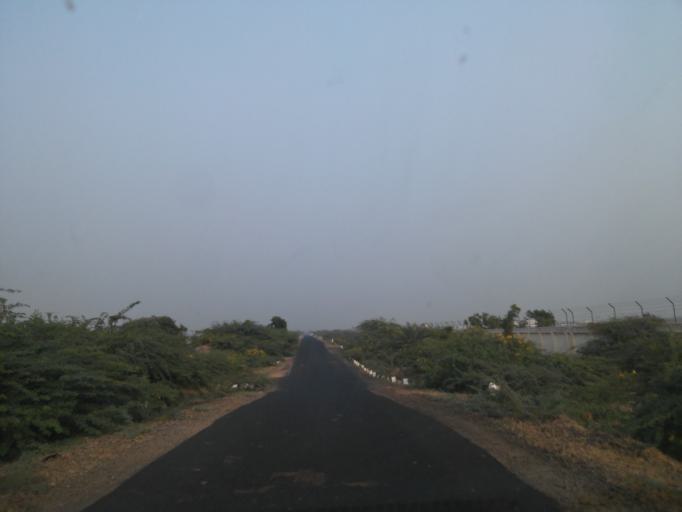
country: IN
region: Gujarat
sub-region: Kachchh
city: Mandvi
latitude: 22.8426
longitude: 69.3067
